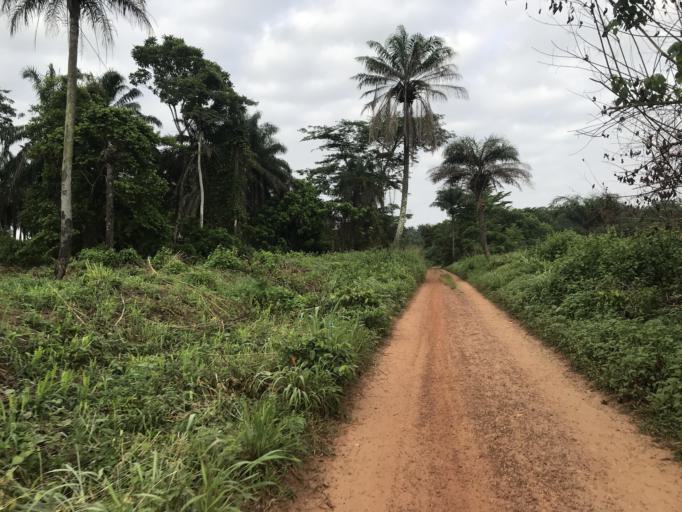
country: SL
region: Eastern Province
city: Pendembu
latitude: 8.0872
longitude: -10.6974
